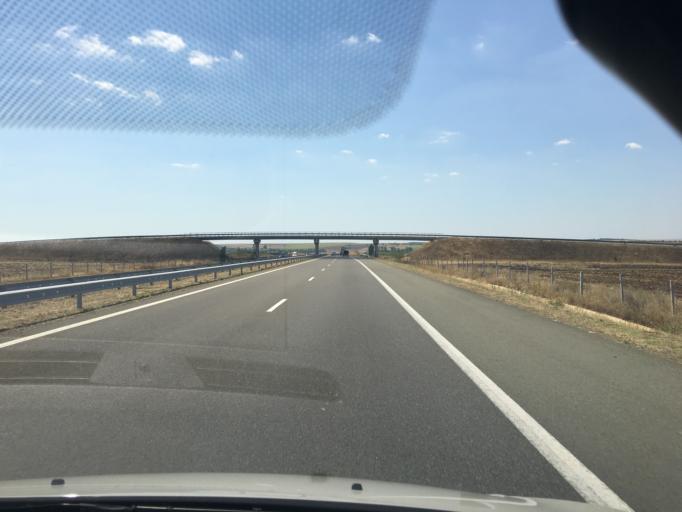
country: BG
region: Burgas
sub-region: Obshtina Karnobat
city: Karnobat
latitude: 42.5838
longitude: 26.9302
